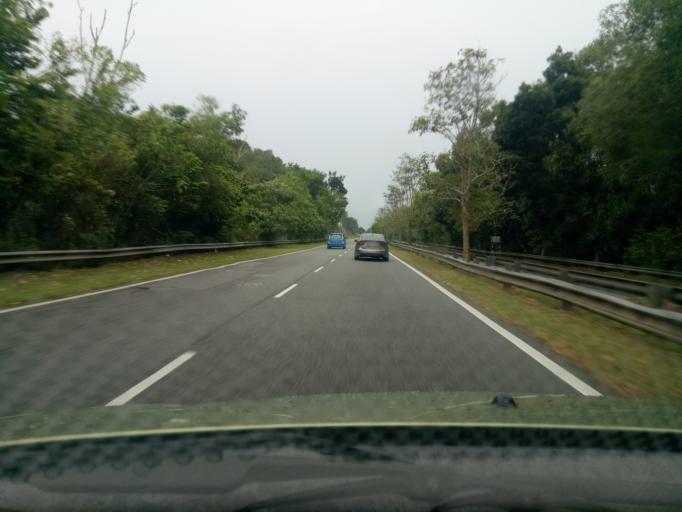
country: MY
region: Kedah
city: Sungai Petani
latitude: 5.6554
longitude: 100.5378
